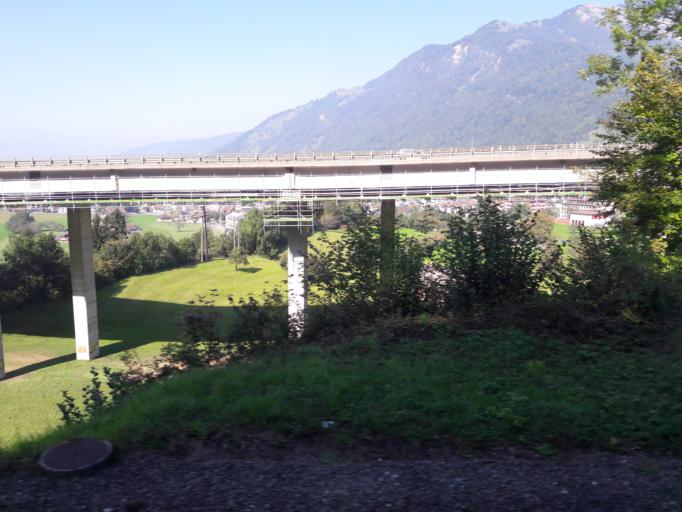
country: CH
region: Schwyz
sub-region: Bezirk Schwyz
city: Goldau
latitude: 47.0494
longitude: 8.5371
